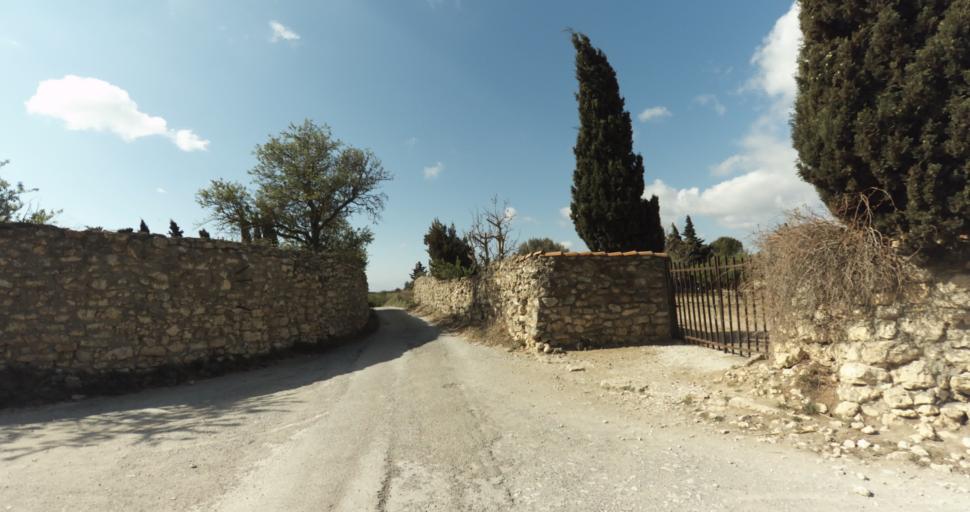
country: FR
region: Languedoc-Roussillon
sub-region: Departement de l'Aude
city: Leucate
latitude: 42.9250
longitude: 3.0372
